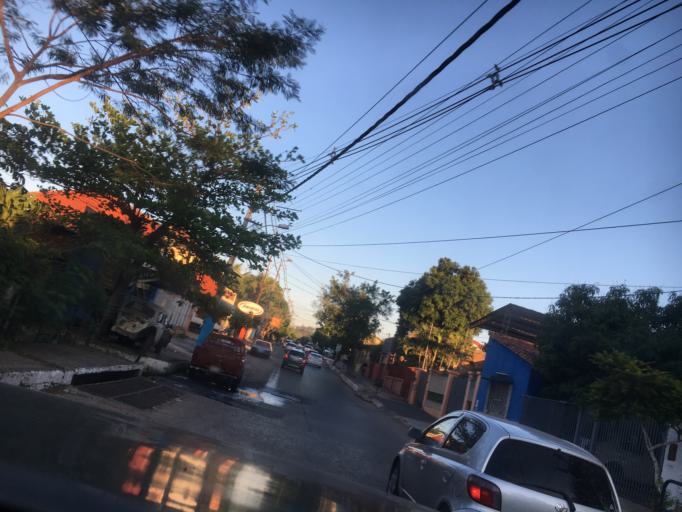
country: PY
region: Asuncion
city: Asuncion
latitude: -25.3102
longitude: -57.6262
